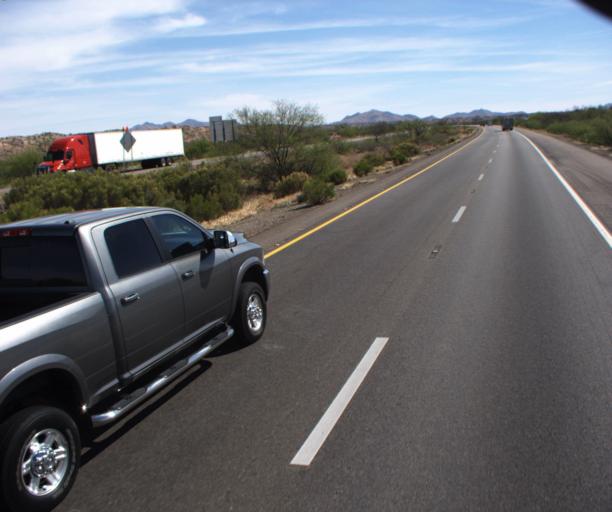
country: US
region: Arizona
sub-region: Cochise County
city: Benson
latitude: 31.9665
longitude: -110.2497
